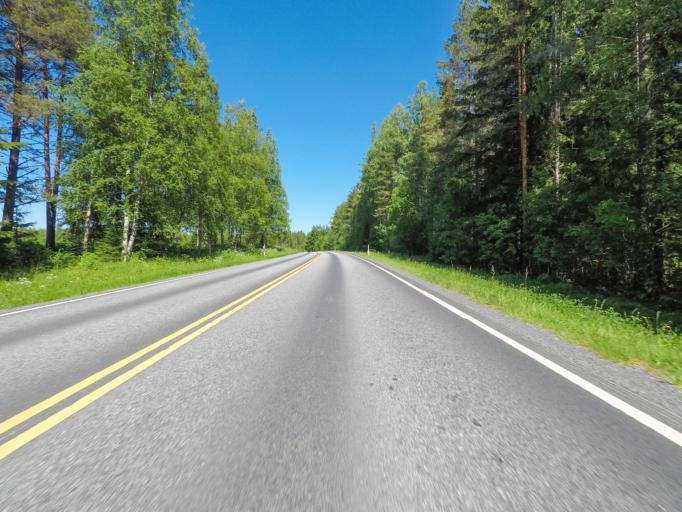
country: FI
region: Southern Savonia
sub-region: Savonlinna
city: Sulkava
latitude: 61.9535
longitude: 28.5178
